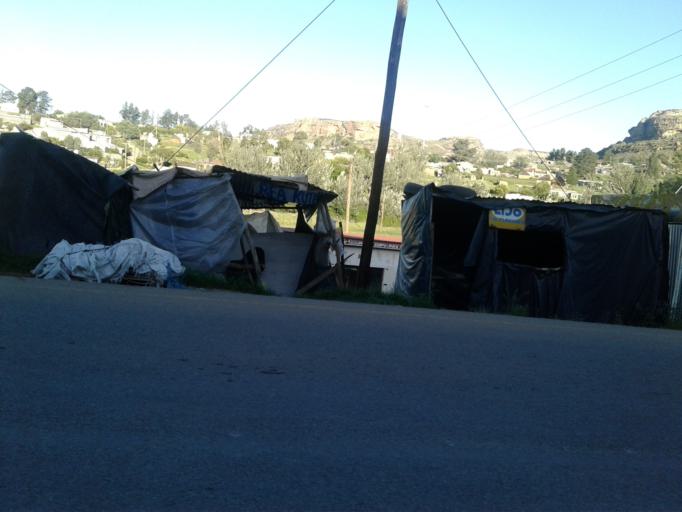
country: LS
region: Butha-Buthe
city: Butha-Buthe
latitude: -28.7656
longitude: 28.2517
